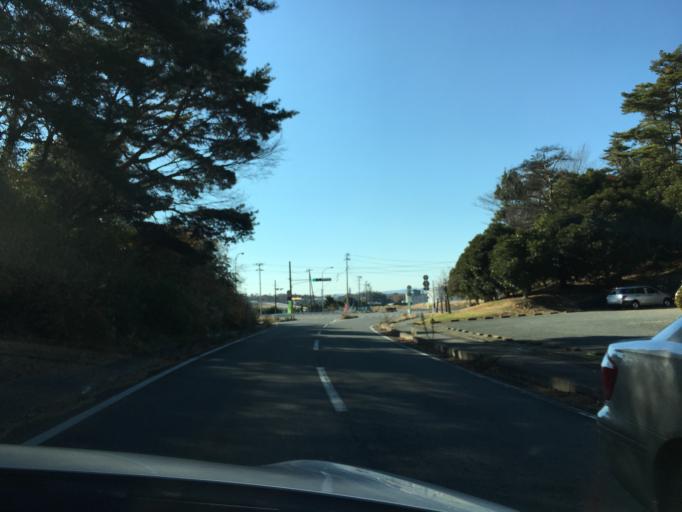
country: JP
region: Fukushima
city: Iwaki
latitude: 36.9324
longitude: 140.8630
